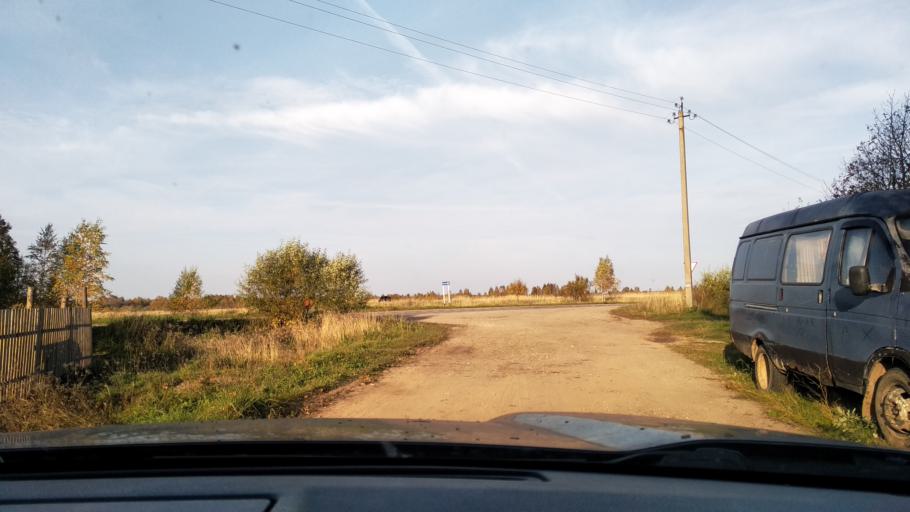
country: RU
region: Tverskaya
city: Krasnyy Kholm
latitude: 58.0094
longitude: 37.1845
